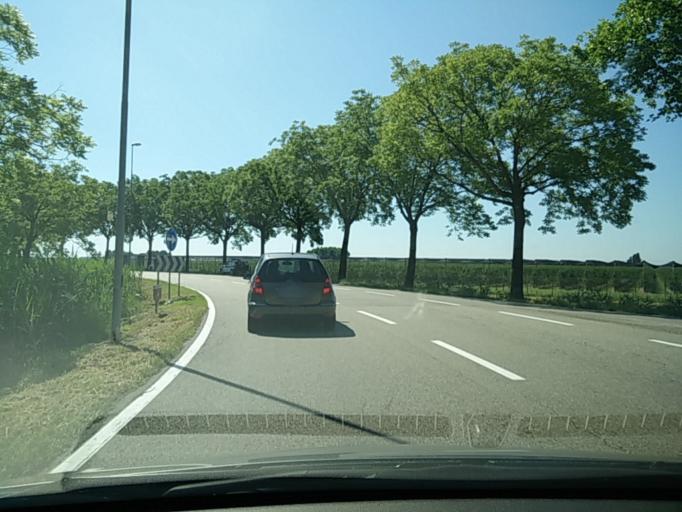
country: IT
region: Veneto
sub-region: Provincia di Venezia
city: San Giorgio di Livenza
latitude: 45.6346
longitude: 12.7463
